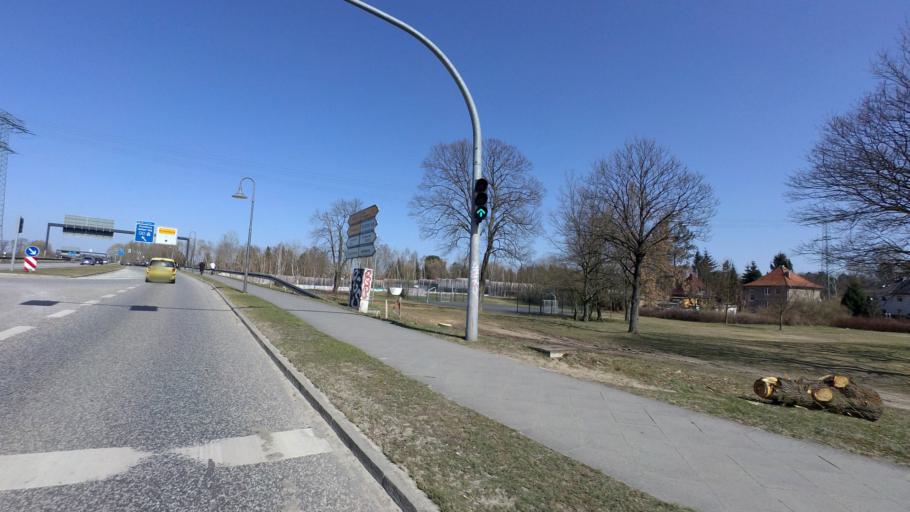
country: DE
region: Brandenburg
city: Birkenwerder
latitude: 52.6987
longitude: 13.2757
